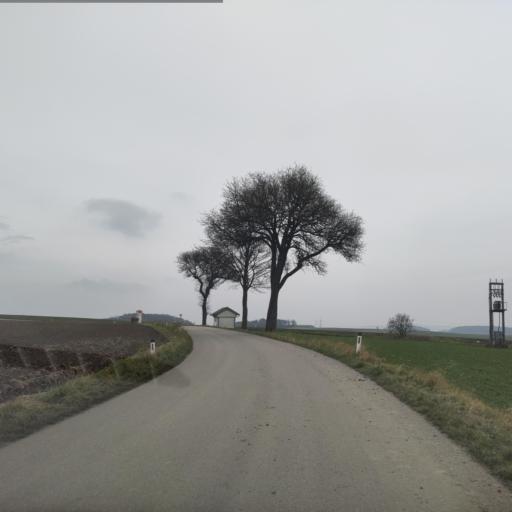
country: AT
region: Lower Austria
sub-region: Politischer Bezirk Sankt Polten
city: Karlstetten
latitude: 48.2463
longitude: 15.5588
